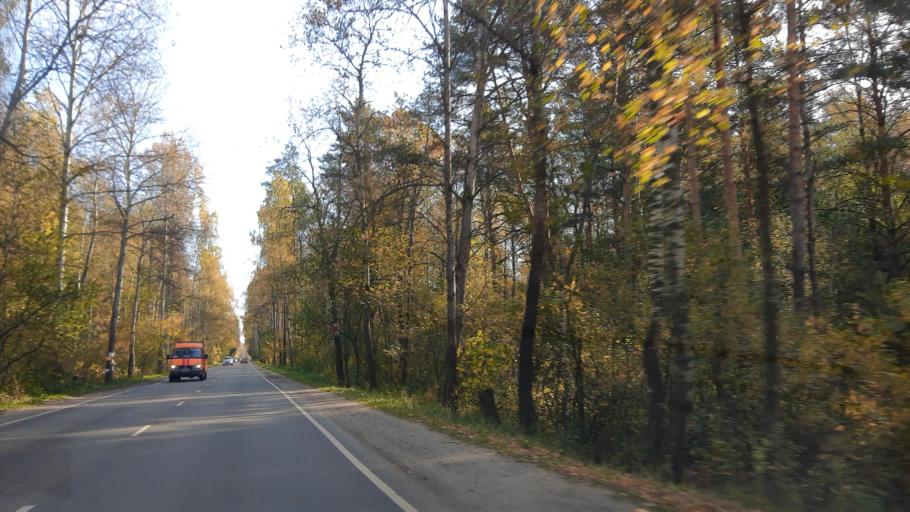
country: RU
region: Moskovskaya
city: Elektrostal'
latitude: 55.8009
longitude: 38.3885
